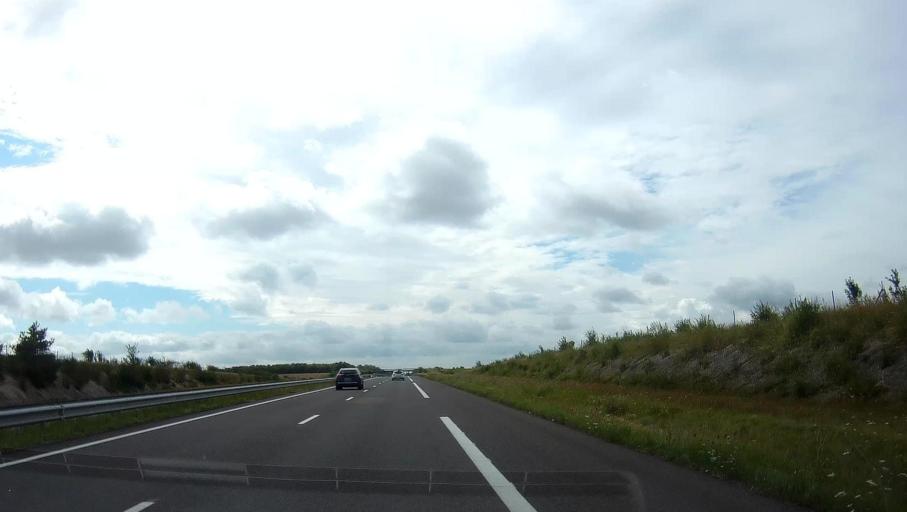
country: FR
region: Champagne-Ardenne
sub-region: Departement de la Marne
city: Fagnieres
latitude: 49.0186
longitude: 4.2921
